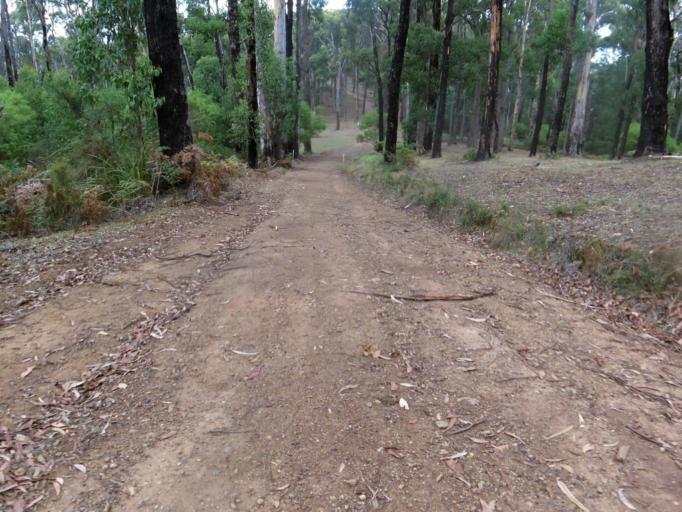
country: AU
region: Victoria
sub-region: Yarra Ranges
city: Healesville
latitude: -37.6126
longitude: 145.5267
